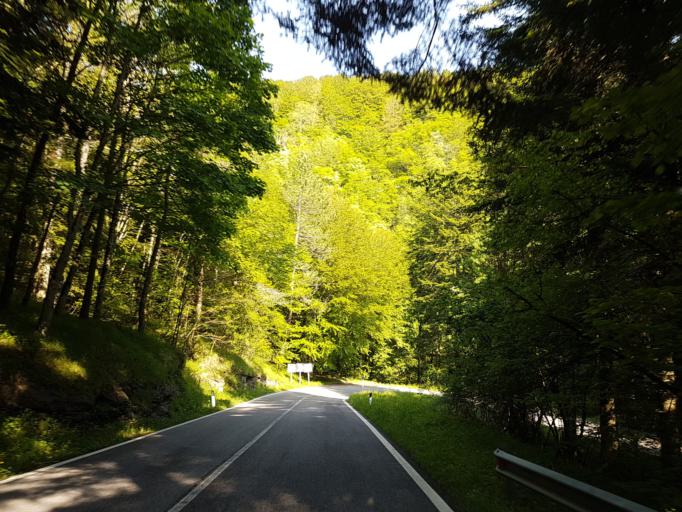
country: IT
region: Tuscany
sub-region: Province of Arezzo
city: Soci
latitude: 43.7961
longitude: 11.8894
